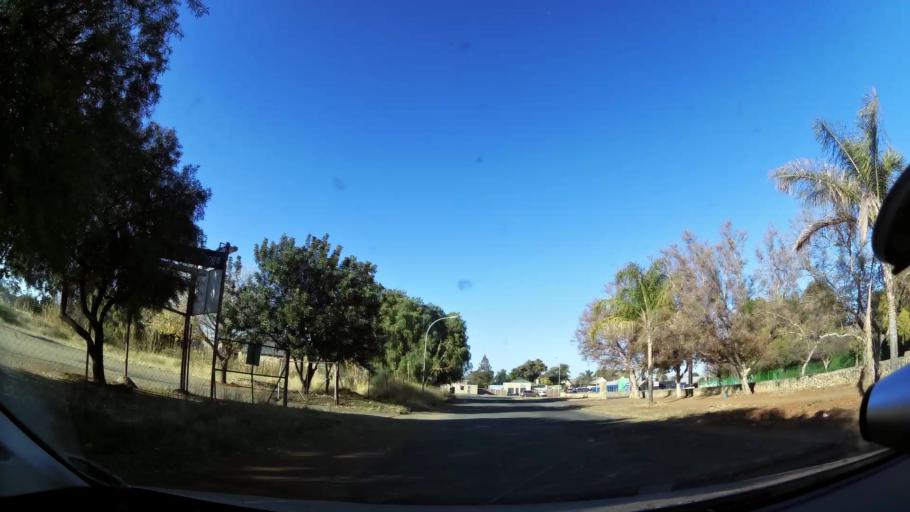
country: ZA
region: Northern Cape
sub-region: Frances Baard District Municipality
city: Kimberley
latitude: -28.7434
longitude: 24.7431
